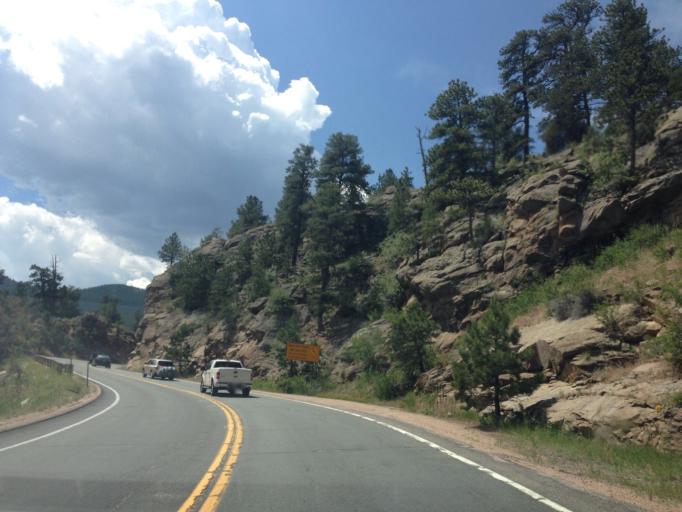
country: US
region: Colorado
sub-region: Larimer County
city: Estes Park
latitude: 40.3792
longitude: -105.4789
